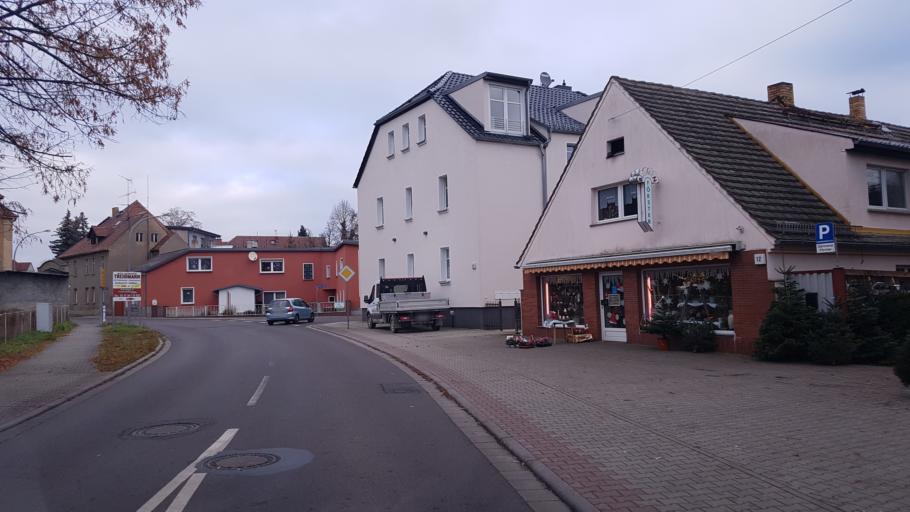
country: DE
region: Brandenburg
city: Schipkau
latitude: 51.5589
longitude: 13.8966
